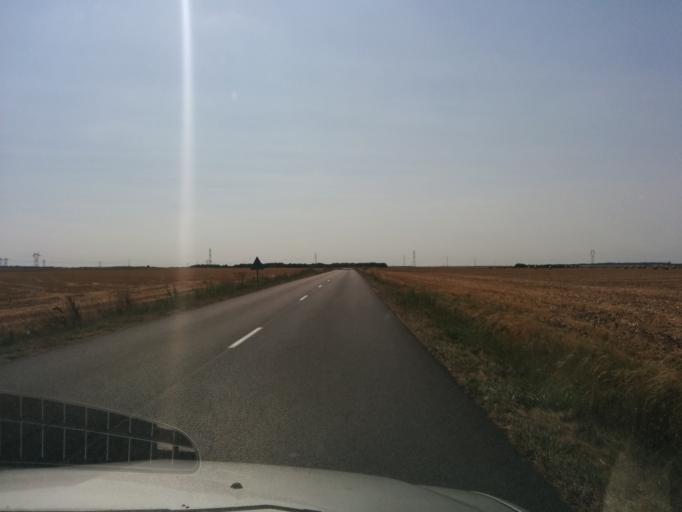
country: FR
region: Poitou-Charentes
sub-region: Departement de la Vienne
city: Moncontour
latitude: 46.8110
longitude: -0.0513
